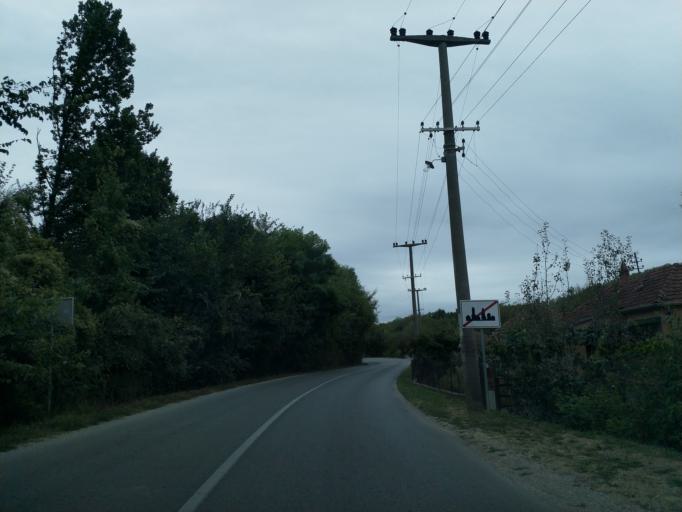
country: RS
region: Central Serbia
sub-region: Pomoravski Okrug
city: Jagodina
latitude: 44.0524
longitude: 21.1808
